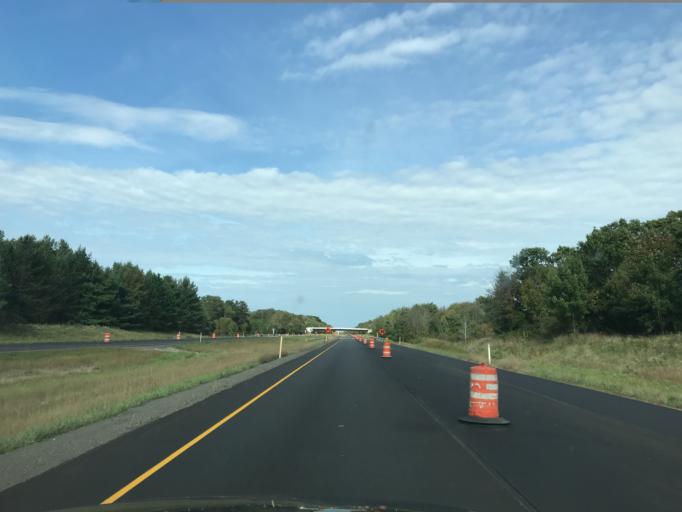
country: US
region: Ohio
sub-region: Ashtabula County
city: Jefferson
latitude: 41.7807
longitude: -80.7318
